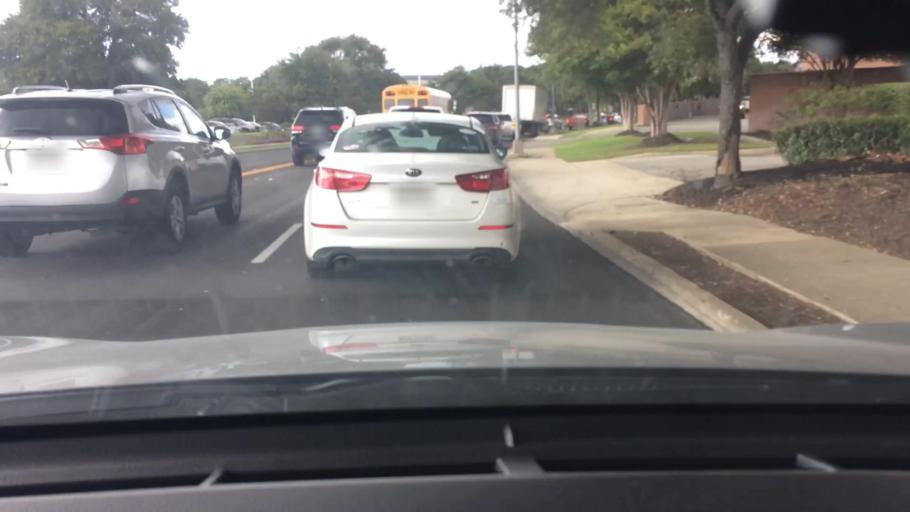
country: US
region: Texas
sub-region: Bexar County
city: Shavano Park
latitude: 29.5612
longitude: -98.5933
